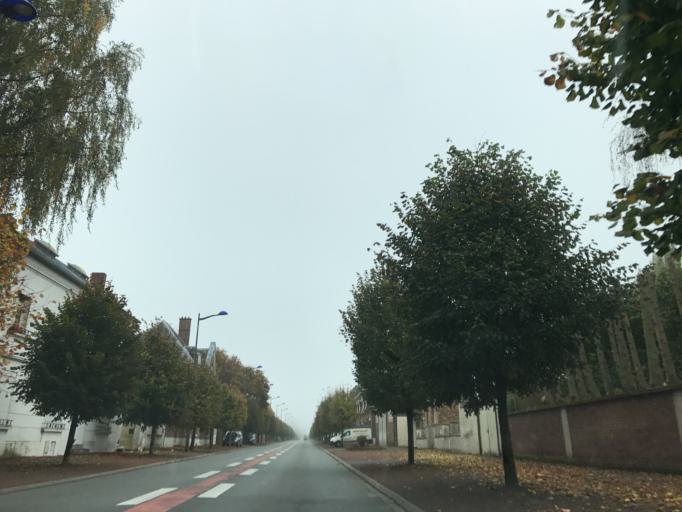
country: FR
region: Nord-Pas-de-Calais
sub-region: Departement du Pas-de-Calais
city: Bapaume
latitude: 50.0974
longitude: 2.8580
